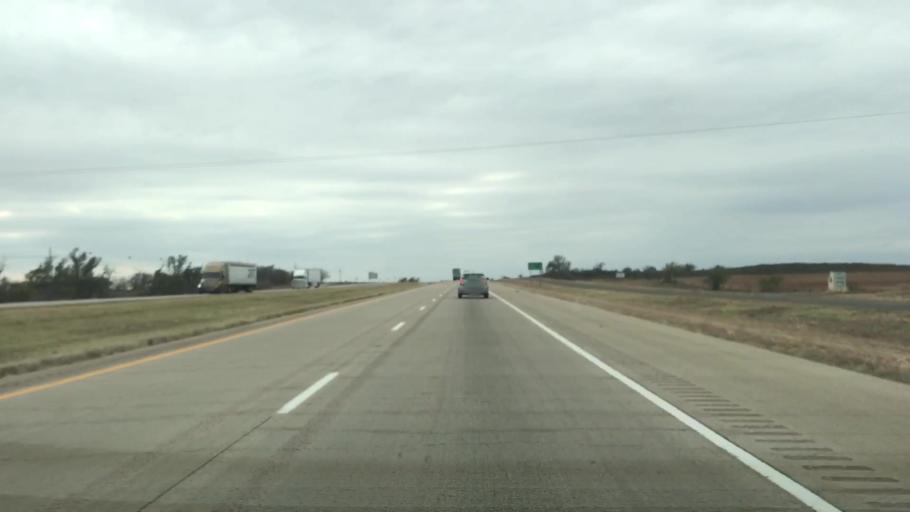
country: US
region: Texas
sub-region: Wheeler County
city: Shamrock
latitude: 35.2270
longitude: -100.1834
